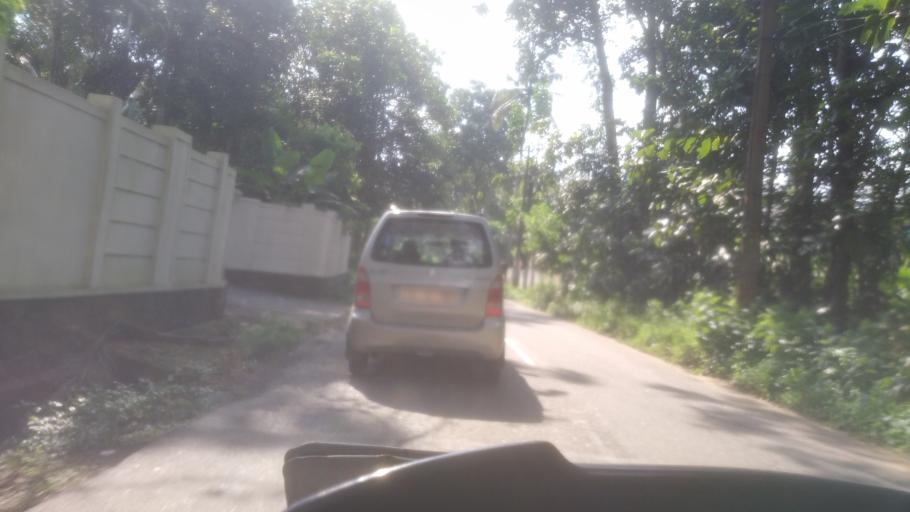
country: IN
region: Kerala
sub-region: Ernakulam
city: Kotamangalam
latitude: 10.0048
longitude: 76.7037
